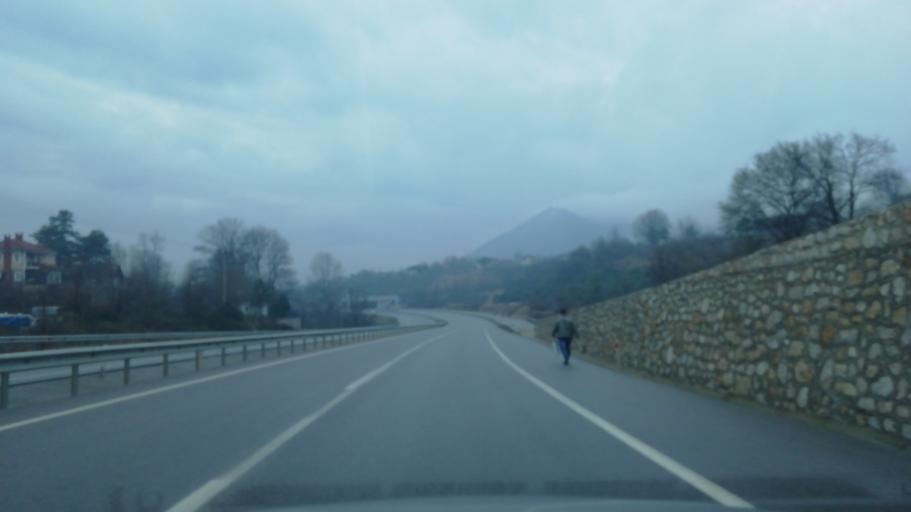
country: TR
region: Sakarya
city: Akyazi
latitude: 40.6277
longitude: 30.6433
